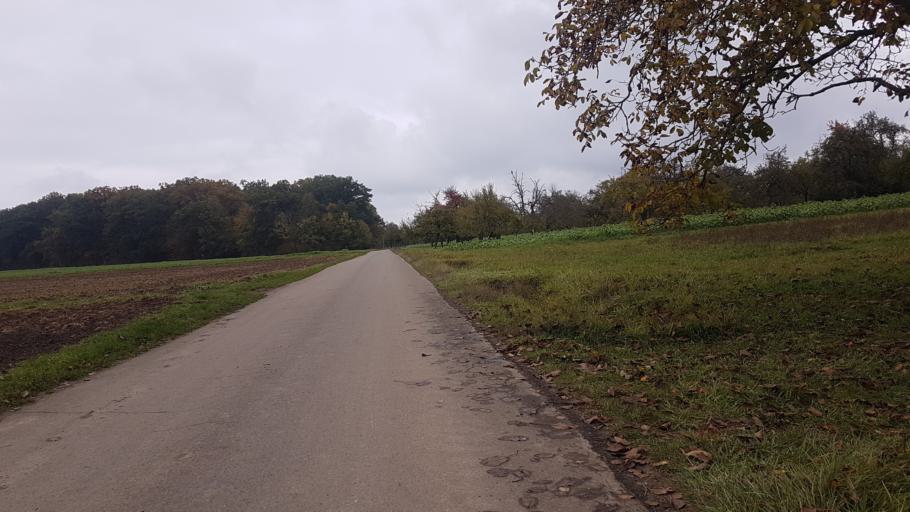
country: DE
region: Baden-Wuerttemberg
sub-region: Tuebingen Region
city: Dusslingen
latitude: 48.4541
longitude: 9.0350
